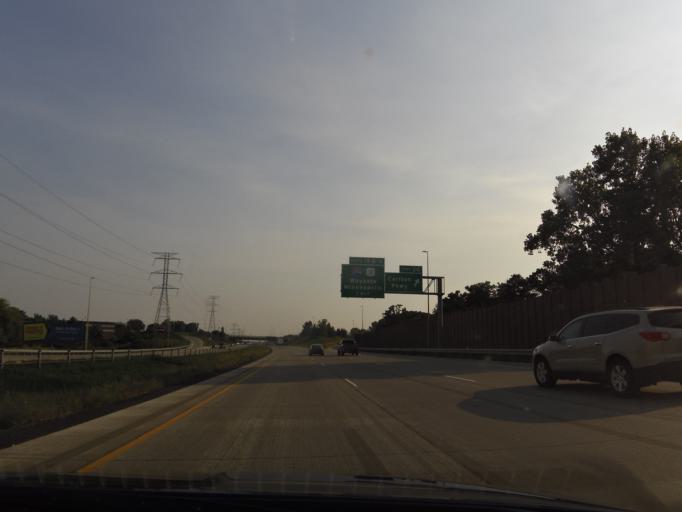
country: US
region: Minnesota
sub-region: Hennepin County
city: Plymouth
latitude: 44.9882
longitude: -93.4595
